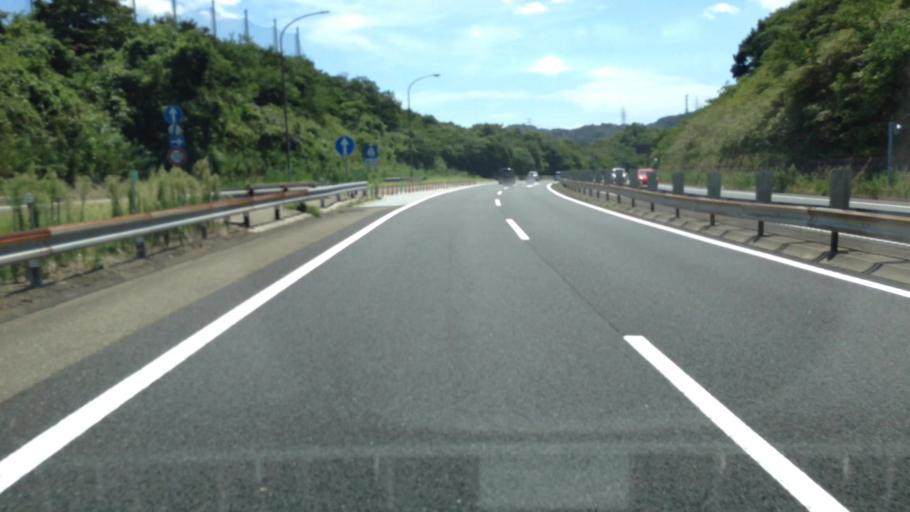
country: JP
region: Kanagawa
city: Yokosuka
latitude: 35.2746
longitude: 139.6349
